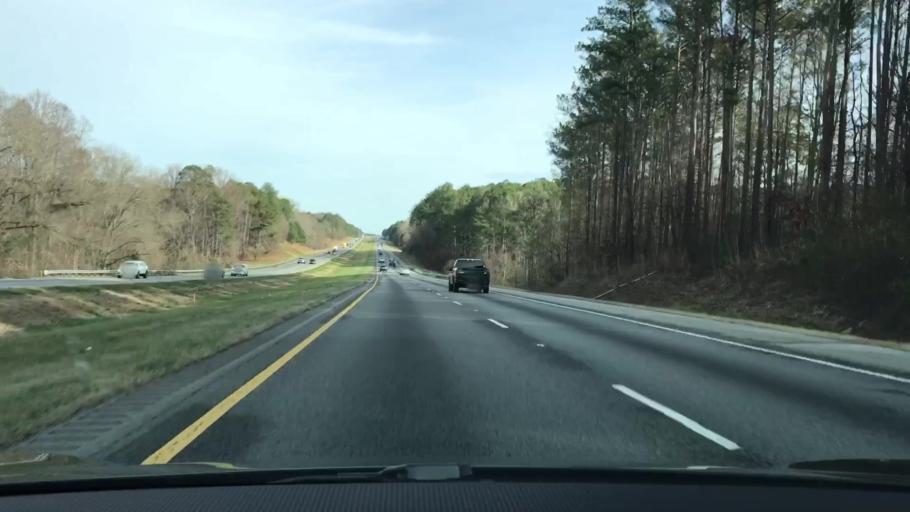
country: US
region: Georgia
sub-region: Newton County
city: Covington
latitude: 33.6099
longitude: -83.7865
